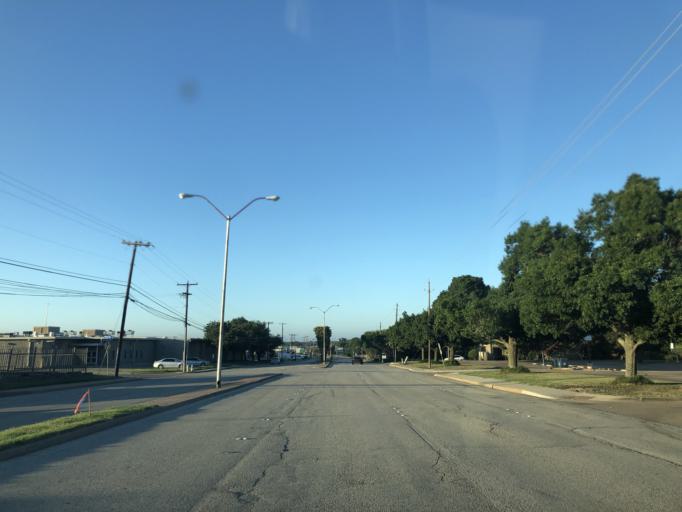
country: US
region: Texas
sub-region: Dallas County
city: Duncanville
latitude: 32.6456
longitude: -96.9255
